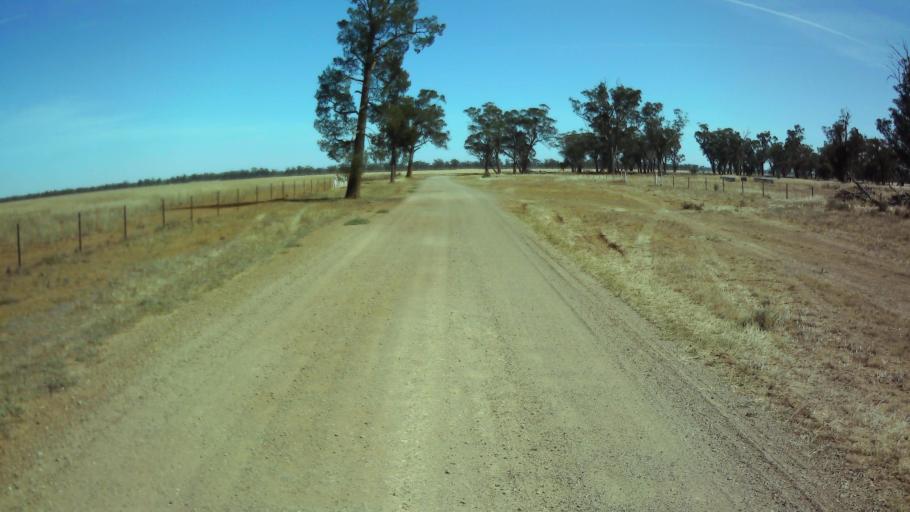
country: AU
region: New South Wales
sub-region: Weddin
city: Grenfell
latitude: -34.1111
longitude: 147.8424
